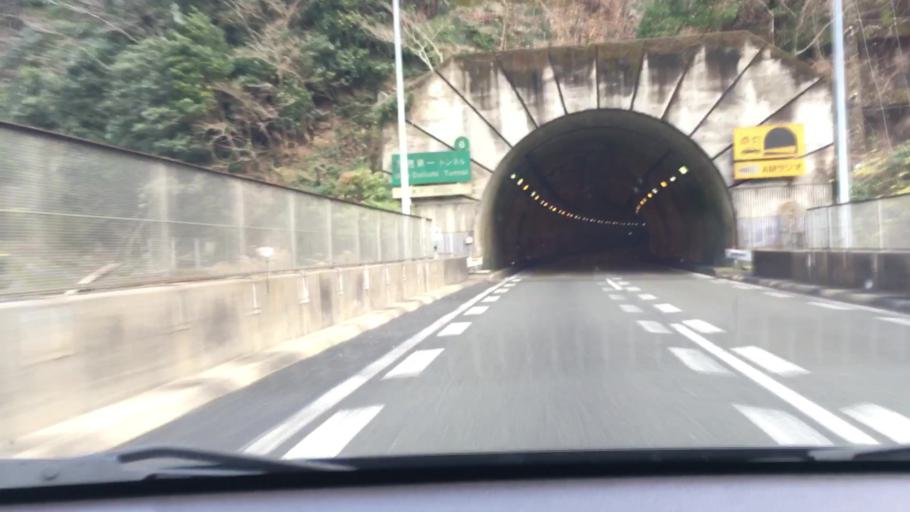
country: JP
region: Kumamoto
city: Hitoyoshi
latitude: 32.3319
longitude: 130.7432
